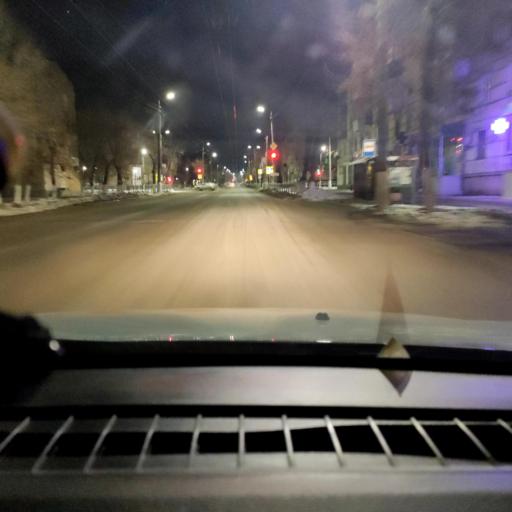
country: RU
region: Samara
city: Novokuybyshevsk
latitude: 53.0918
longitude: 49.9498
